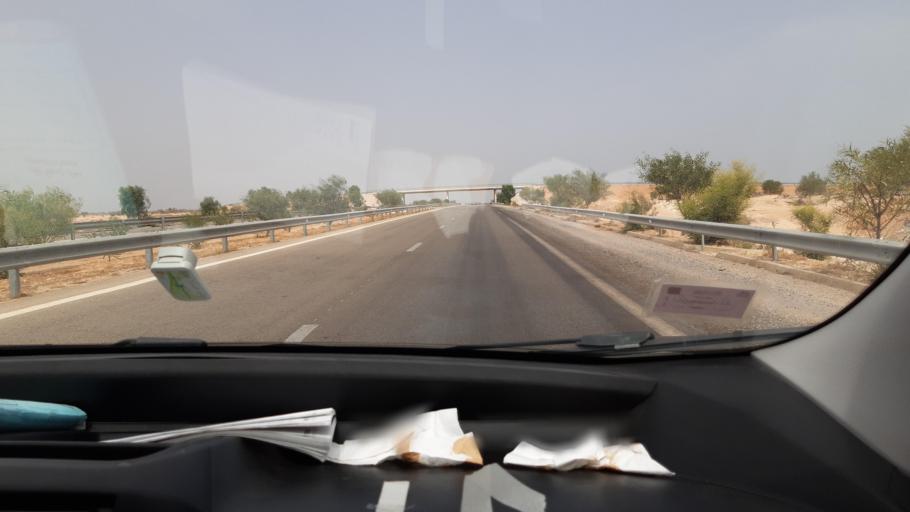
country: TN
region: Safaqis
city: Sfax
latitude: 34.8414
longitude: 10.6683
